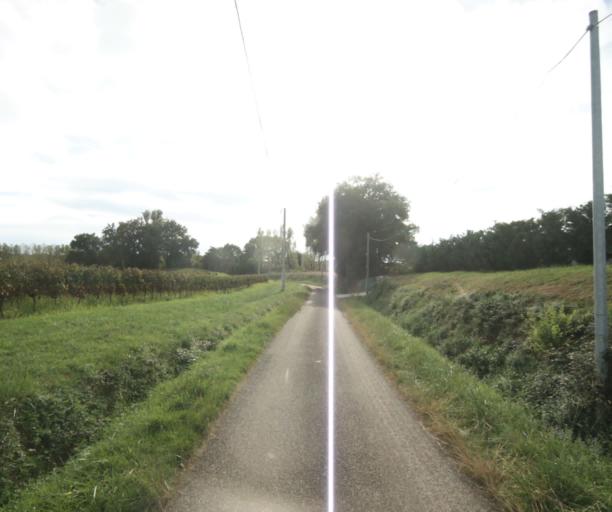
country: FR
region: Midi-Pyrenees
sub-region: Departement du Gers
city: Cazaubon
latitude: 43.8687
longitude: -0.1207
